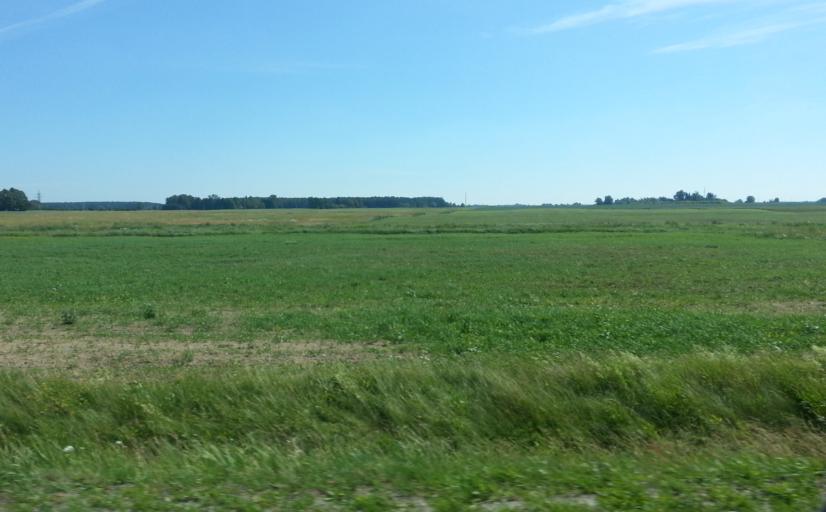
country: LT
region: Panevezys
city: Pasvalys
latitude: 55.9137
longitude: 24.3358
